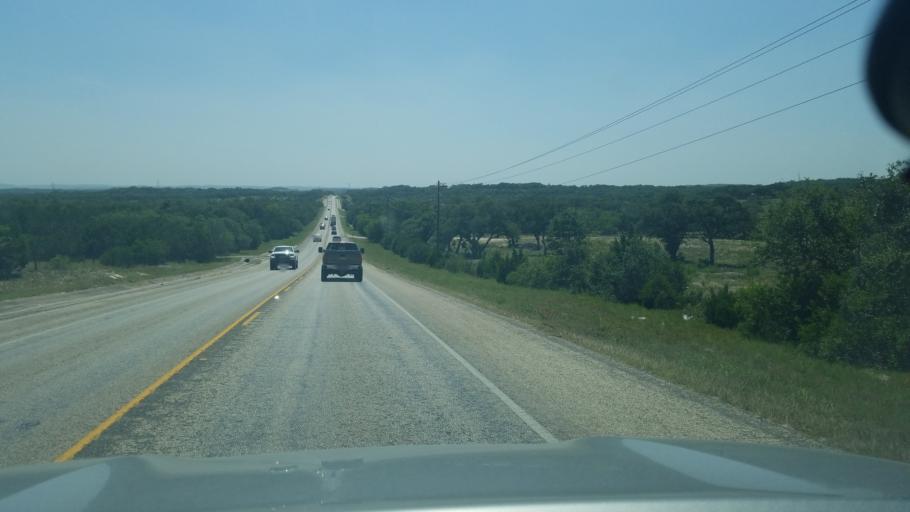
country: US
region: Texas
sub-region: Bexar County
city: Fair Oaks Ranch
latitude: 29.8118
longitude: -98.6325
